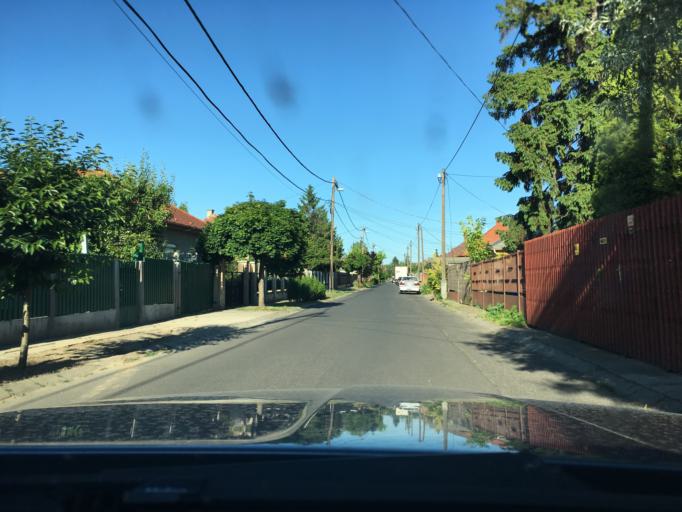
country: HU
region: Hajdu-Bihar
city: Debrecen
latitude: 47.5391
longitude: 21.6608
